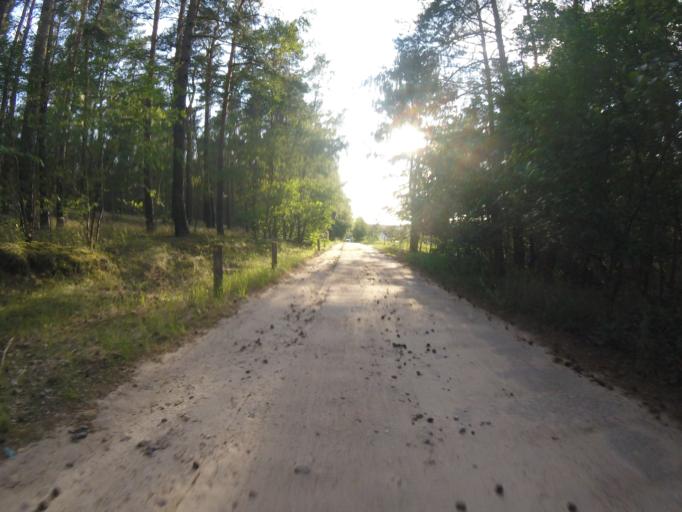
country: DE
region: Brandenburg
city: Schwerin
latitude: 52.1986
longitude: 13.5926
